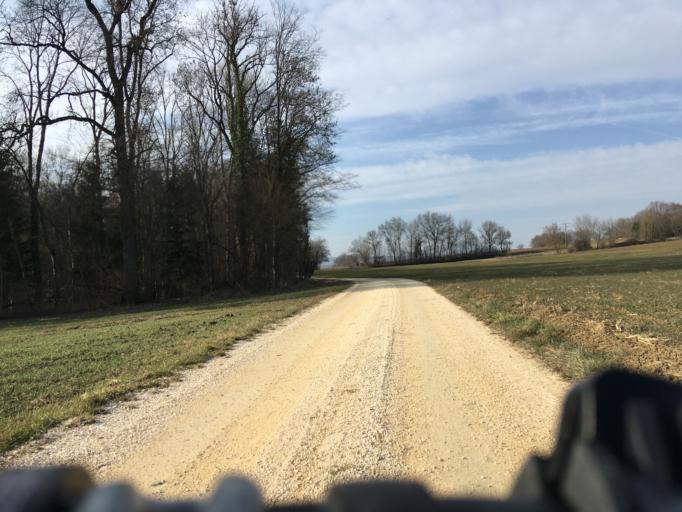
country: CH
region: Schaffhausen
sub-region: Bezirk Reiat
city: Thayngen
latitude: 47.7720
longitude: 8.7255
